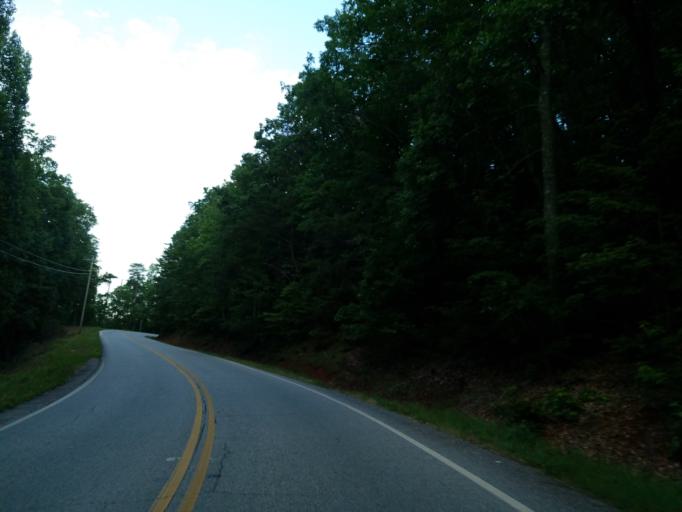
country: US
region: Georgia
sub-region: Lumpkin County
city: Dahlonega
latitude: 34.6058
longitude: -83.9698
